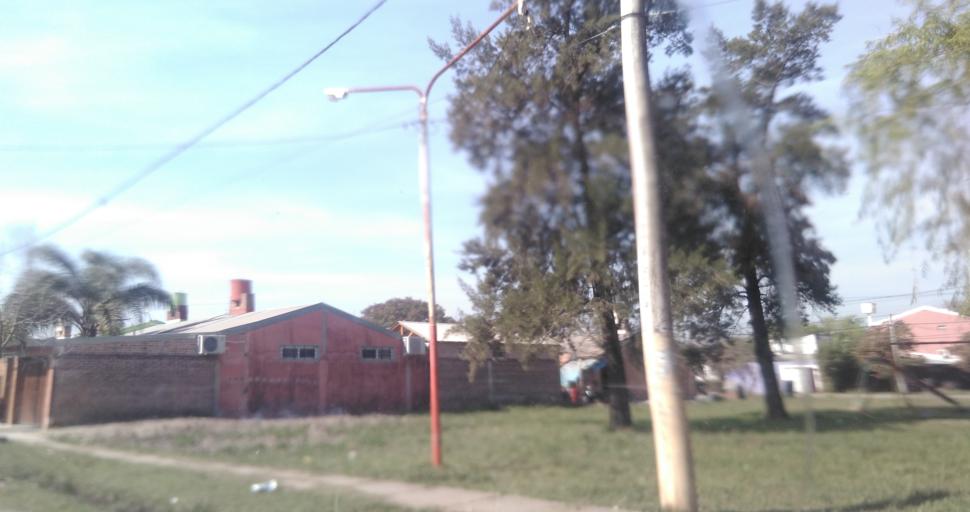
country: AR
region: Chaco
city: Fontana
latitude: -27.4468
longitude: -59.0364
